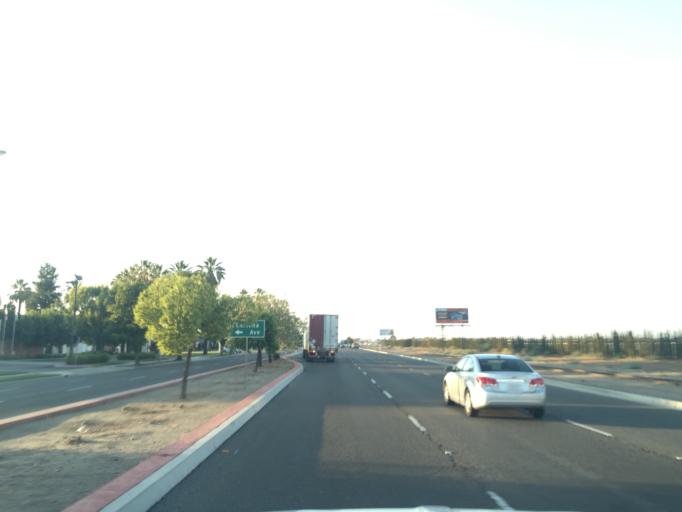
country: US
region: California
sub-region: Fresno County
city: Sunnyside
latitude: 36.7593
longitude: -119.7004
